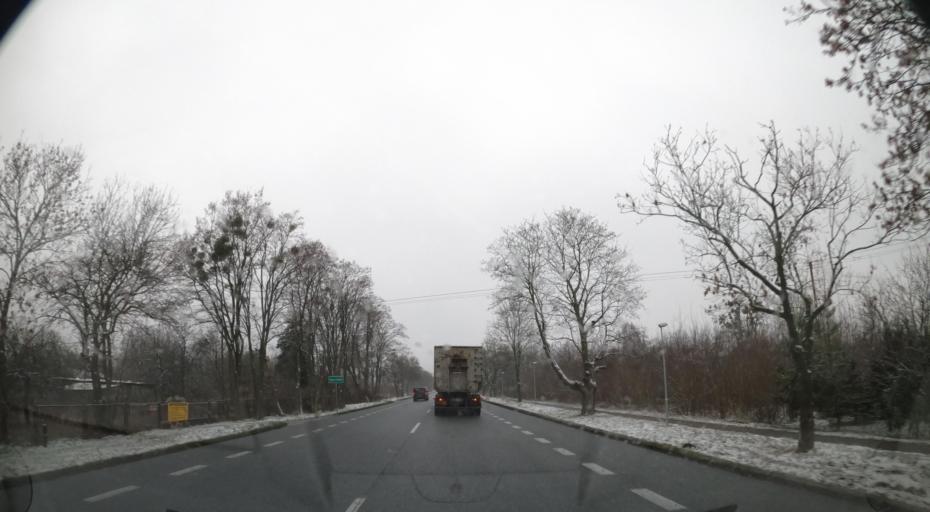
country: PL
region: Masovian Voivodeship
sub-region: Powiat sochaczewski
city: Teresin
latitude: 52.2178
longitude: 20.3661
